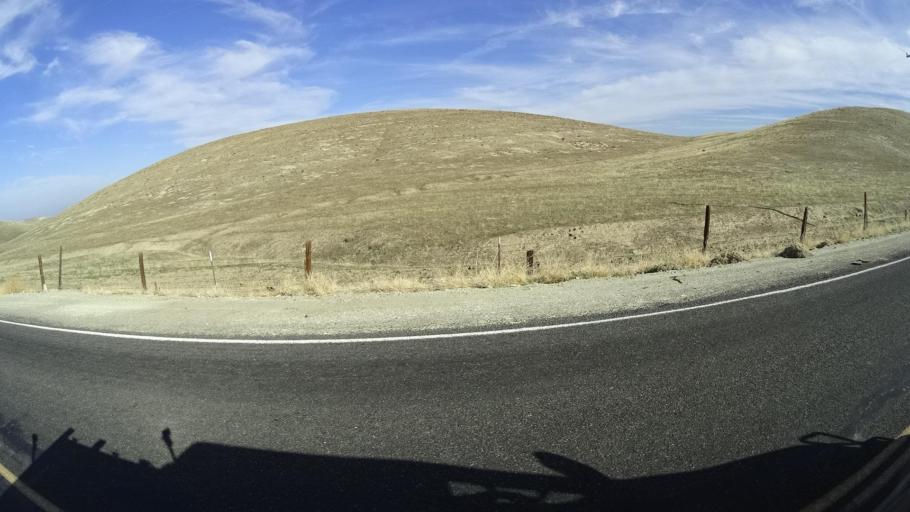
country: US
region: California
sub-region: Kern County
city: Oildale
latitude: 35.6099
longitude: -118.9103
